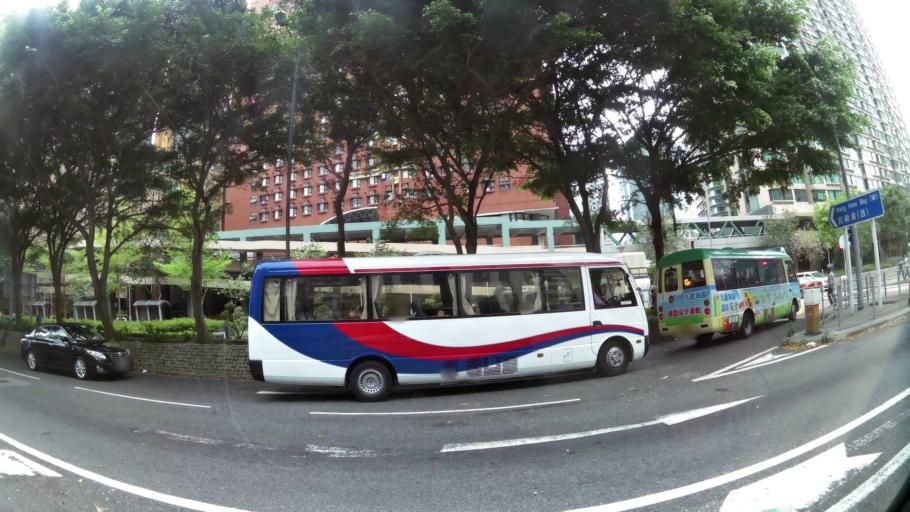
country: HK
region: Kowloon City
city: Kowloon
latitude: 22.3047
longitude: 114.1861
